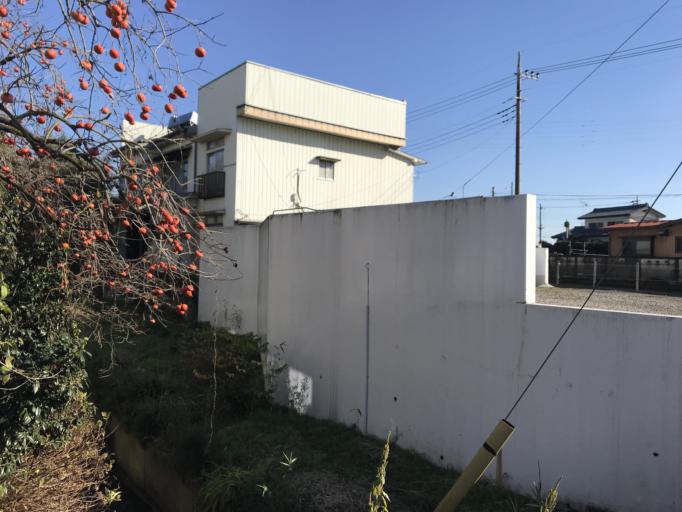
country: JP
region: Ibaraki
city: Sakai
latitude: 36.1524
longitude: 139.8119
